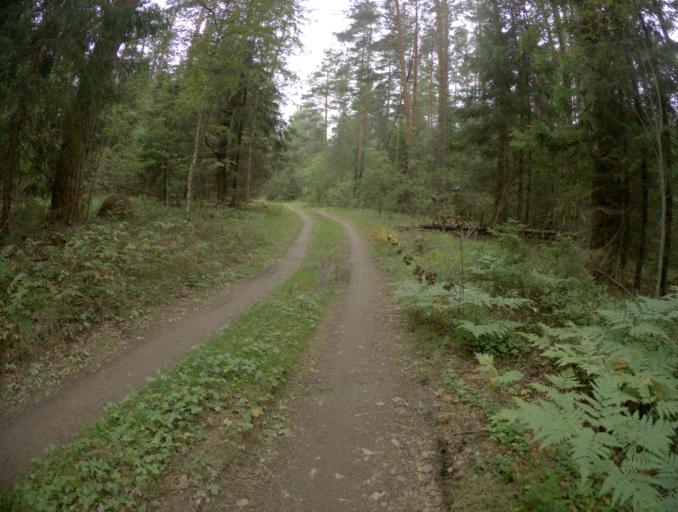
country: RU
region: Vladimir
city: Raduzhnyy
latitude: 55.9846
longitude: 40.2836
